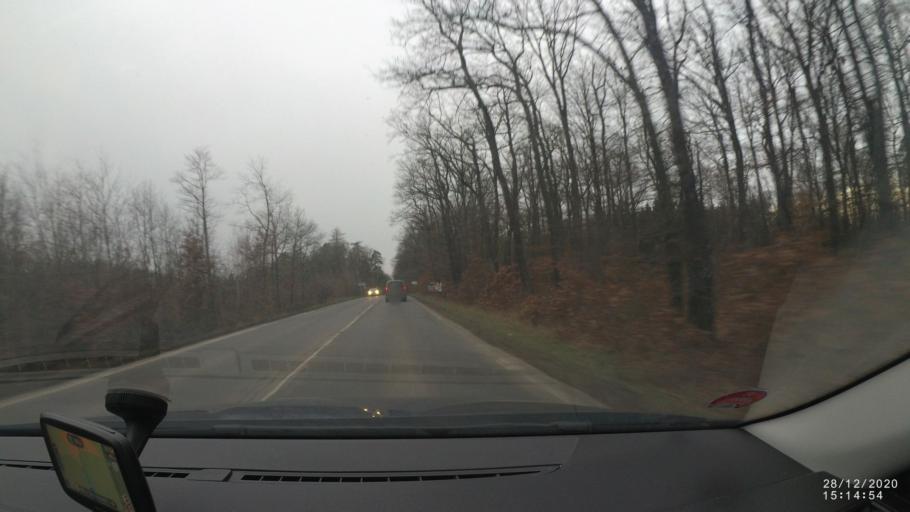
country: CZ
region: Central Bohemia
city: Uvaly
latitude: 50.0718
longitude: 14.6924
